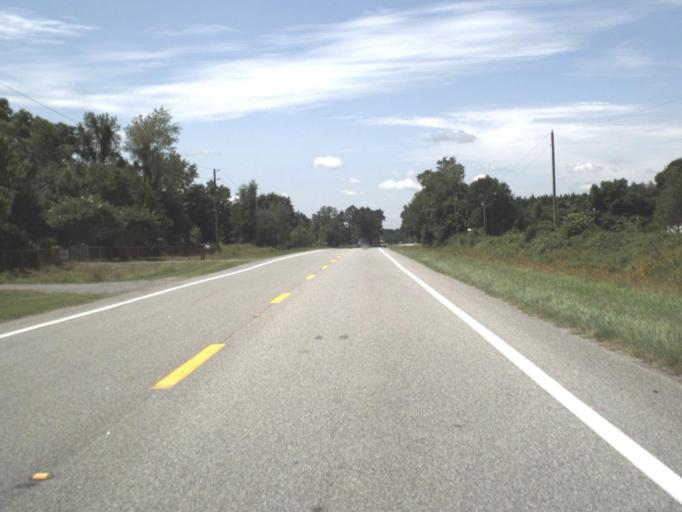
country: US
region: Florida
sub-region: Hamilton County
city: Jasper
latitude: 30.4143
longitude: -82.9337
